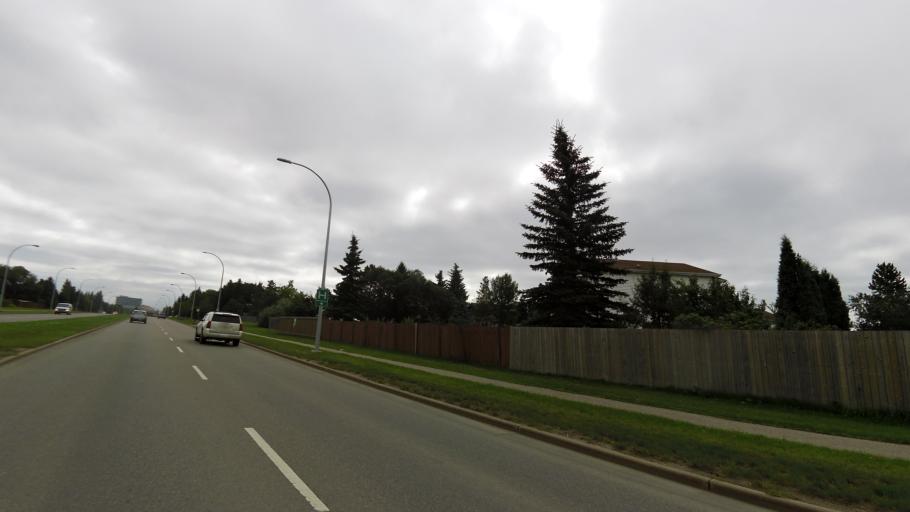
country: CA
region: Alberta
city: St. Albert
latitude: 53.5213
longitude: -113.6480
